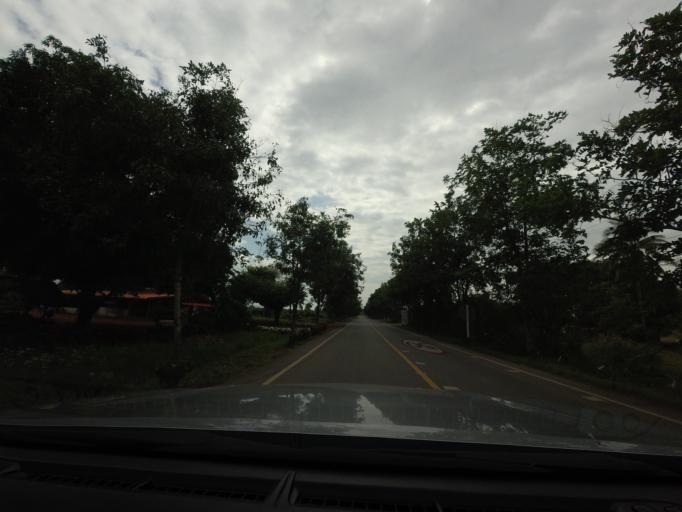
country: TH
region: Phitsanulok
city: Noen Maprang
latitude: 16.6137
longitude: 100.6196
